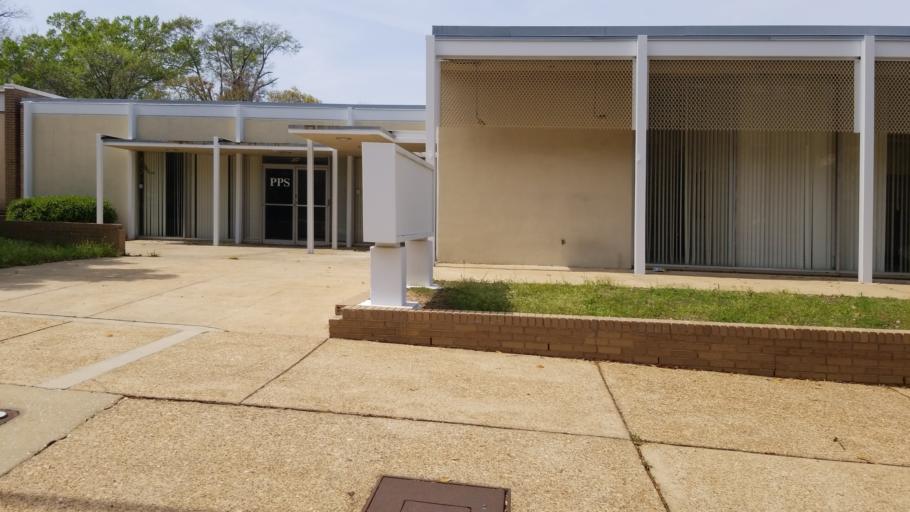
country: US
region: Alabama
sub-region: Montgomery County
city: Montgomery
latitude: 32.3707
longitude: -86.3088
